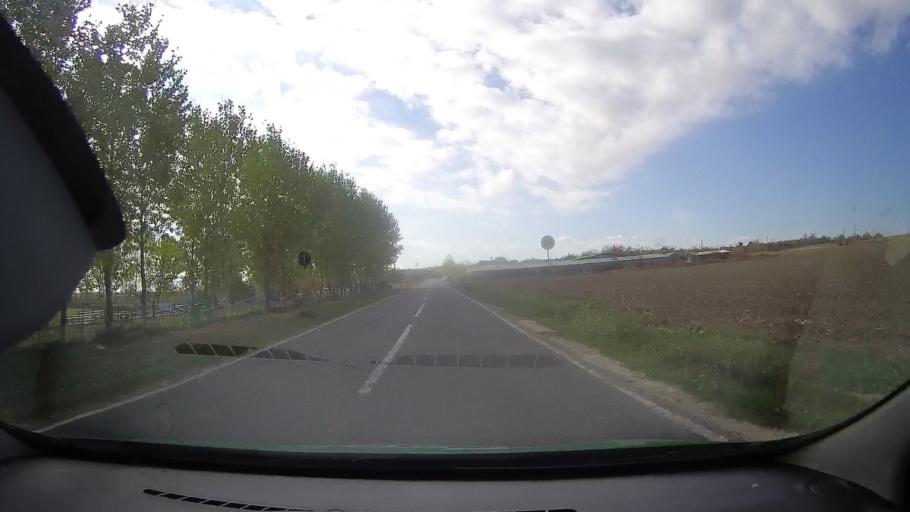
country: RO
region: Tulcea
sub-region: Comuna Sarichioi
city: Sarichioi
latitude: 44.9586
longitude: 28.8577
